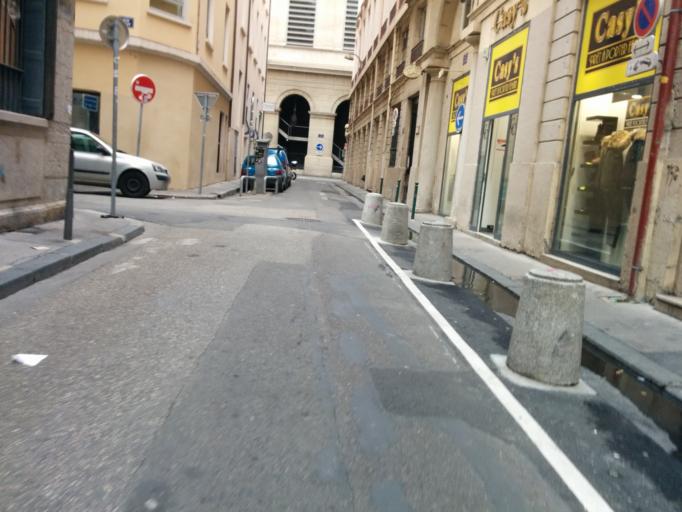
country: FR
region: Rhone-Alpes
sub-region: Departement du Rhone
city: Lyon
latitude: 45.7671
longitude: 4.8368
